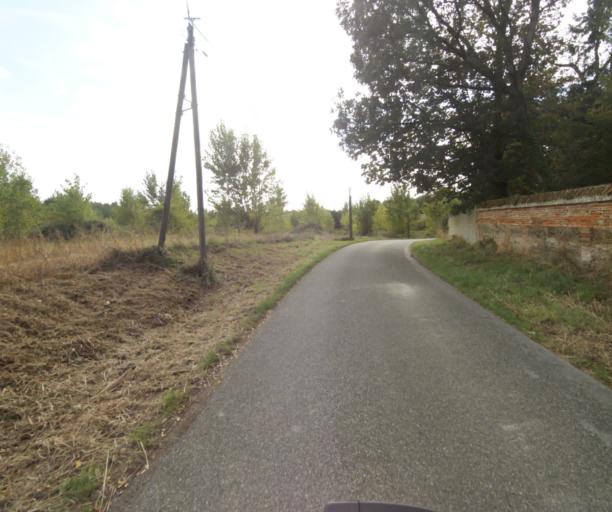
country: FR
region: Midi-Pyrenees
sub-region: Departement du Tarn-et-Garonne
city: Finhan
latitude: 43.9268
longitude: 1.2180
